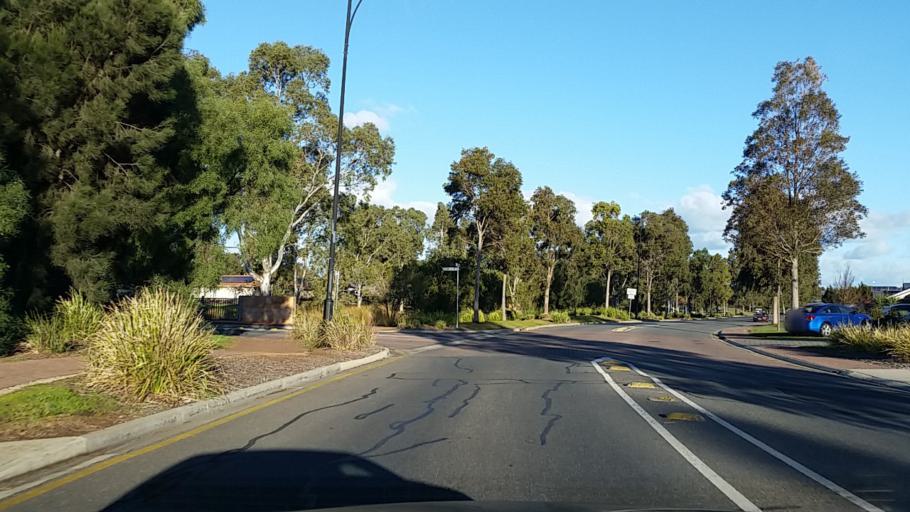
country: AU
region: South Australia
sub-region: Playford
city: Smithfield
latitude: -34.6843
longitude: 138.6798
